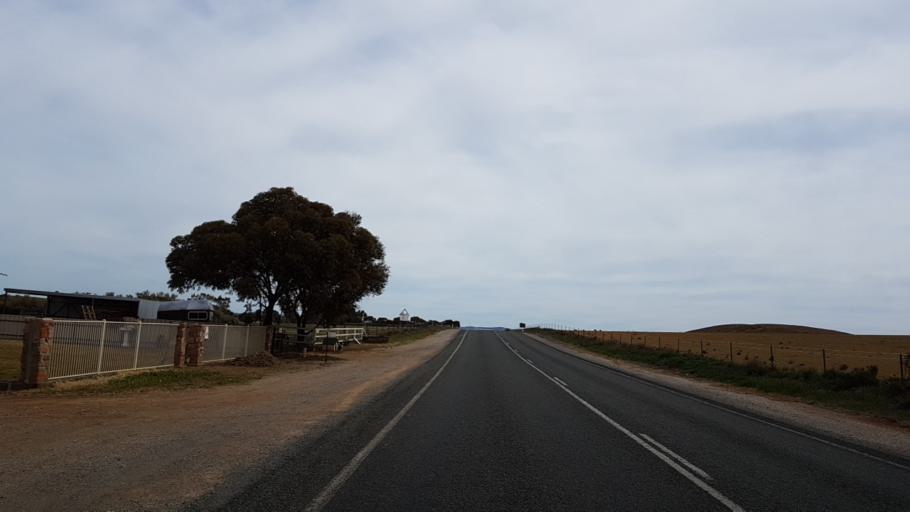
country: AU
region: South Australia
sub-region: Peterborough
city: Peterborough
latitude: -33.0300
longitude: 138.7410
